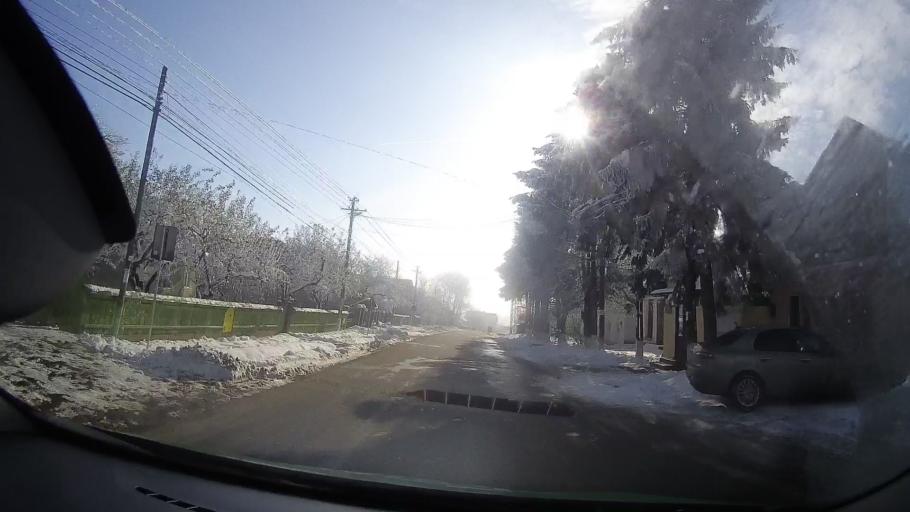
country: RO
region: Iasi
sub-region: Comuna Cristesti
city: Cristesti
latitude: 47.2589
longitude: 26.5749
